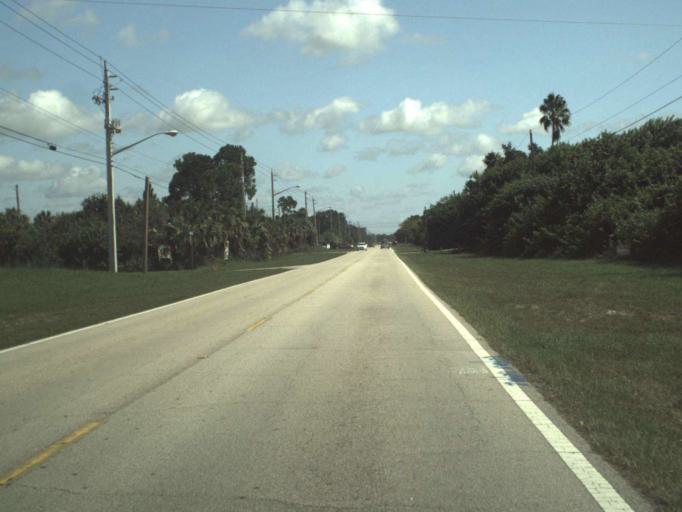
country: US
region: Florida
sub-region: Saint Lucie County
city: Port Saint Lucie
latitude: 27.2370
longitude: -80.3769
